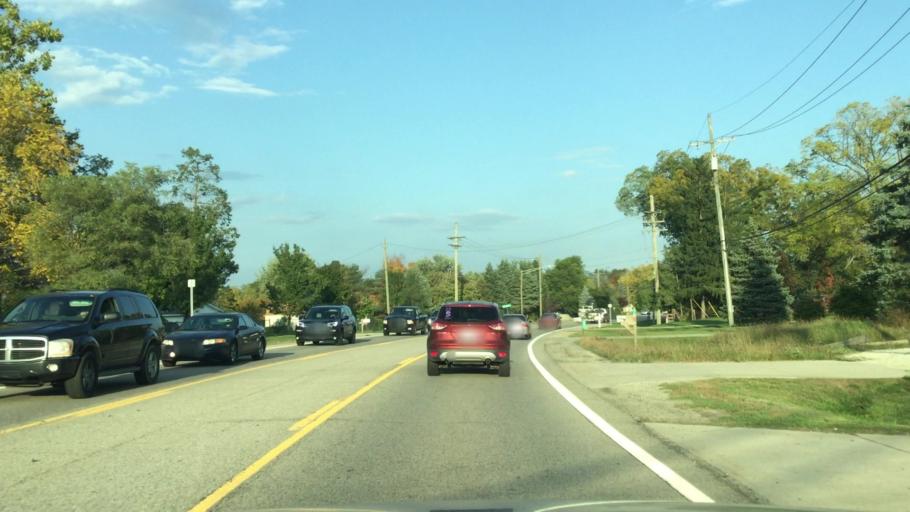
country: US
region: Michigan
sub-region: Oakland County
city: West Bloomfield Township
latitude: 42.6195
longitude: -83.4101
